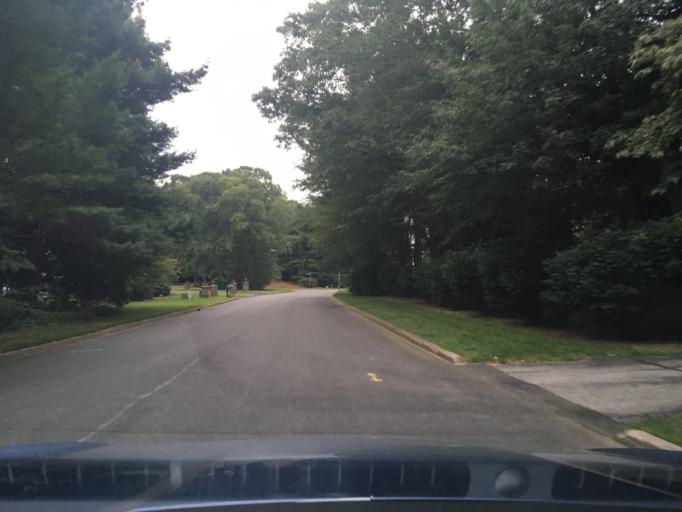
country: US
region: Rhode Island
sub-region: Kent County
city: East Greenwich
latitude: 41.6333
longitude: -71.5016
